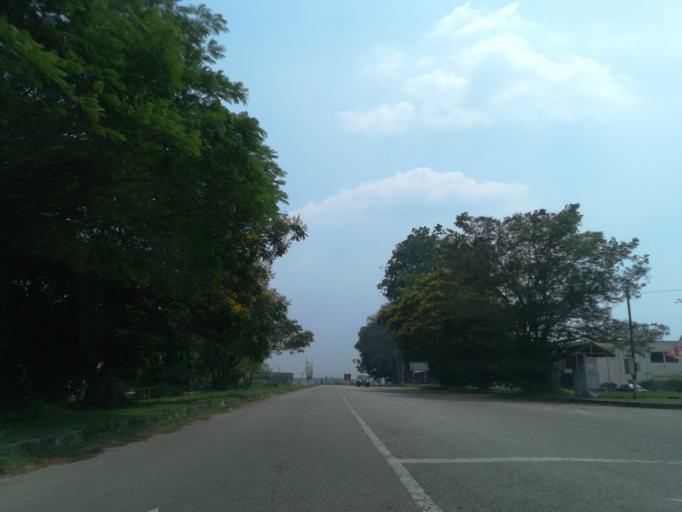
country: MY
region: Penang
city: Tasek Glugor
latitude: 5.4420
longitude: 100.5374
